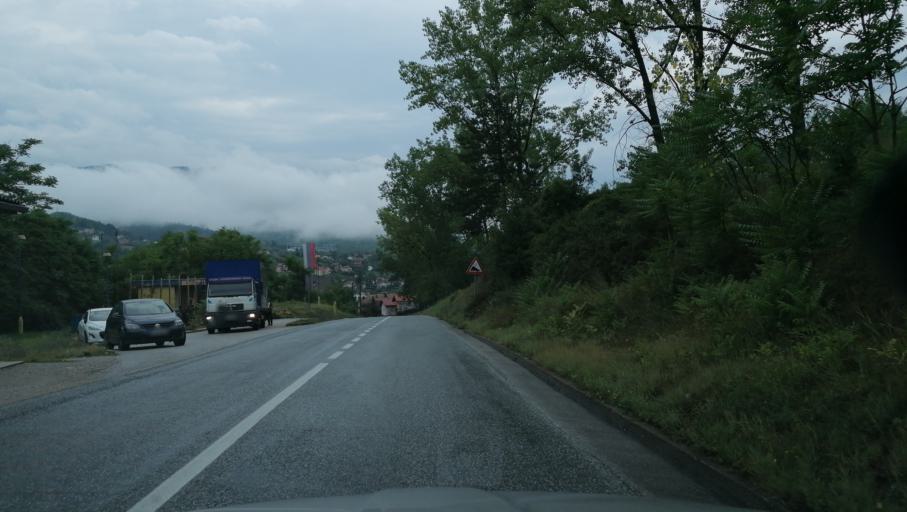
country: BA
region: Republika Srpska
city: Visegrad
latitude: 43.7833
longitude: 19.3002
